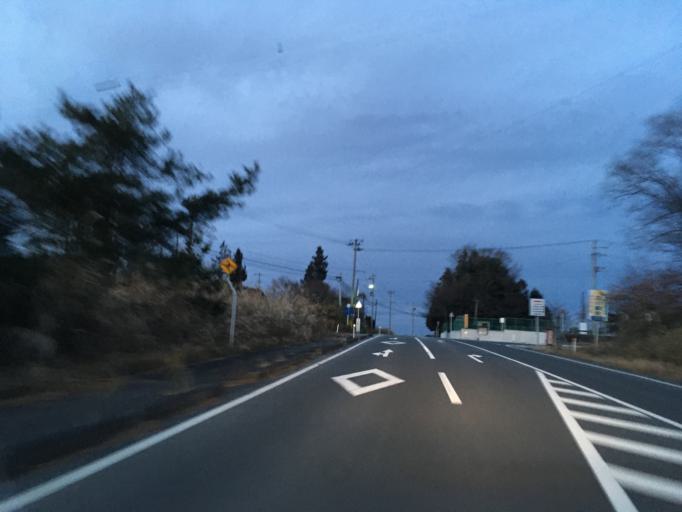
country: JP
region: Miyagi
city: Kogota
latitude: 38.6937
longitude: 141.0953
